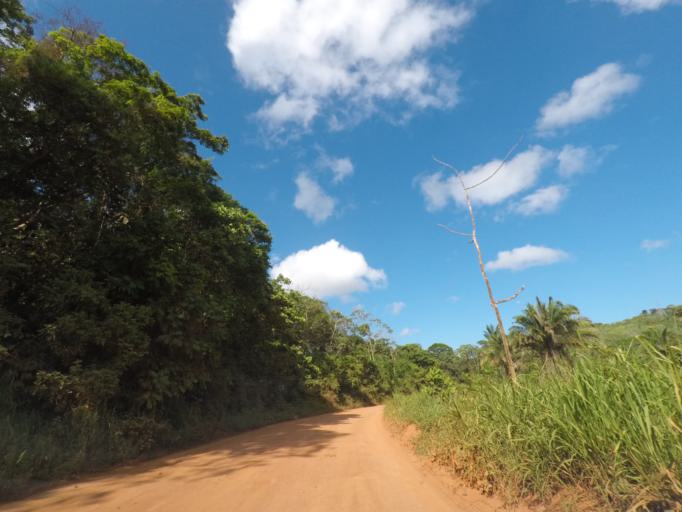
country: BR
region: Bahia
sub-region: Itacare
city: Itacare
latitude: -14.2136
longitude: -39.0573
